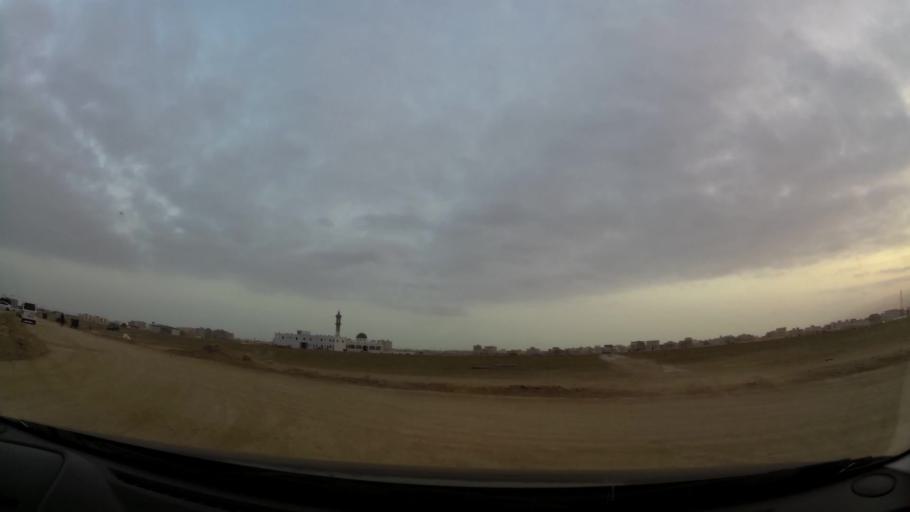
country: OM
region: Zufar
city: Salalah
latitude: 17.0372
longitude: 54.0314
